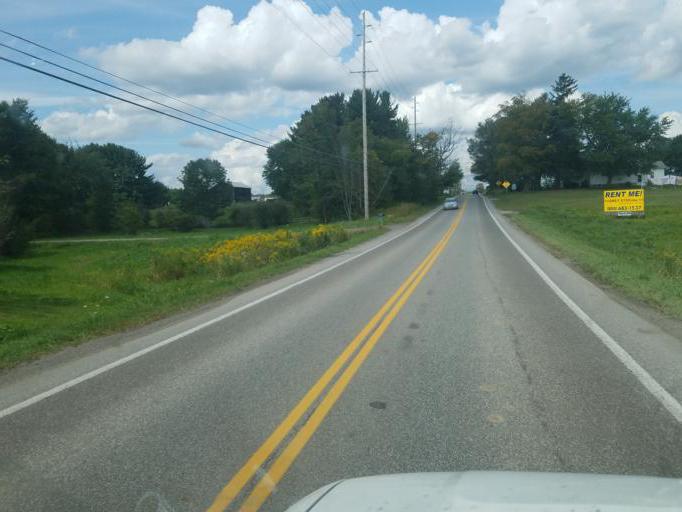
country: US
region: Ohio
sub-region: Geauga County
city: Middlefield
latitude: 41.4411
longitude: -81.0634
